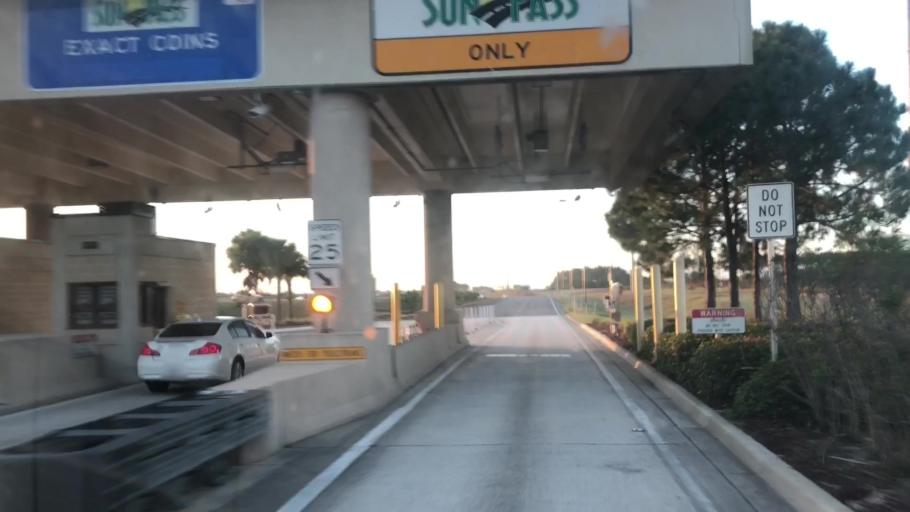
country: US
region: Florida
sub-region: Polk County
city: Citrus Ridge
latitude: 28.4173
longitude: -81.6320
